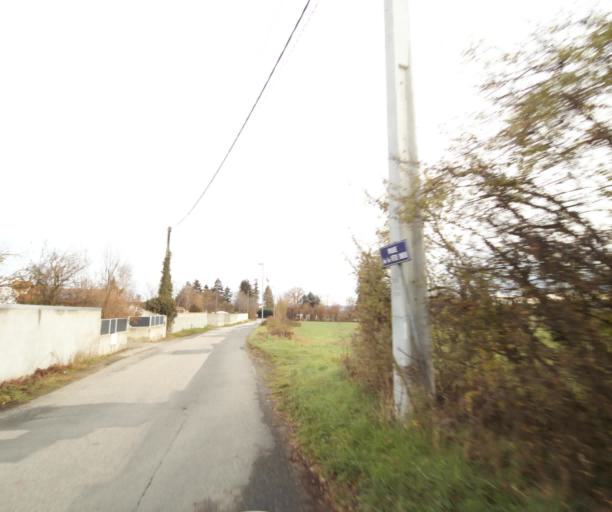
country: FR
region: Rhone-Alpes
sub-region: Departement de la Loire
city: Sury-le-Comtal
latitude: 45.5300
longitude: 4.1931
